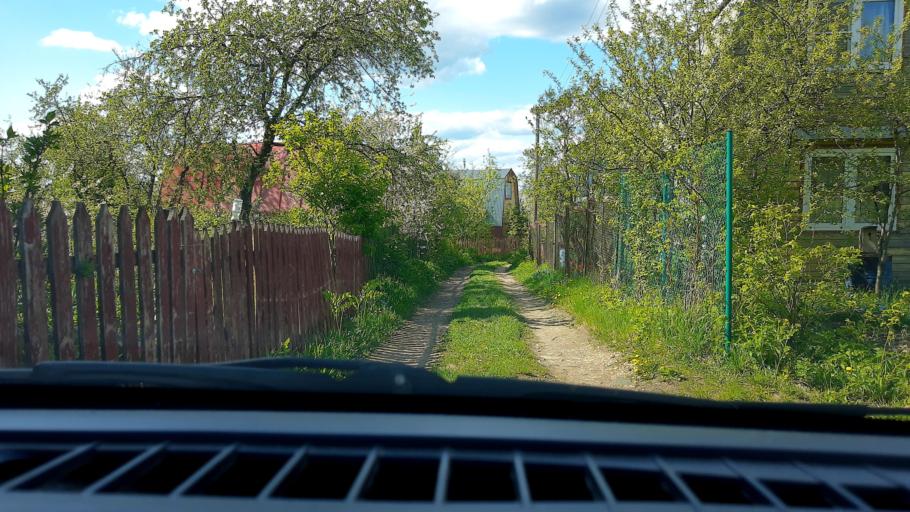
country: RU
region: Nizjnij Novgorod
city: Nizhniy Novgorod
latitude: 56.2190
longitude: 43.9122
